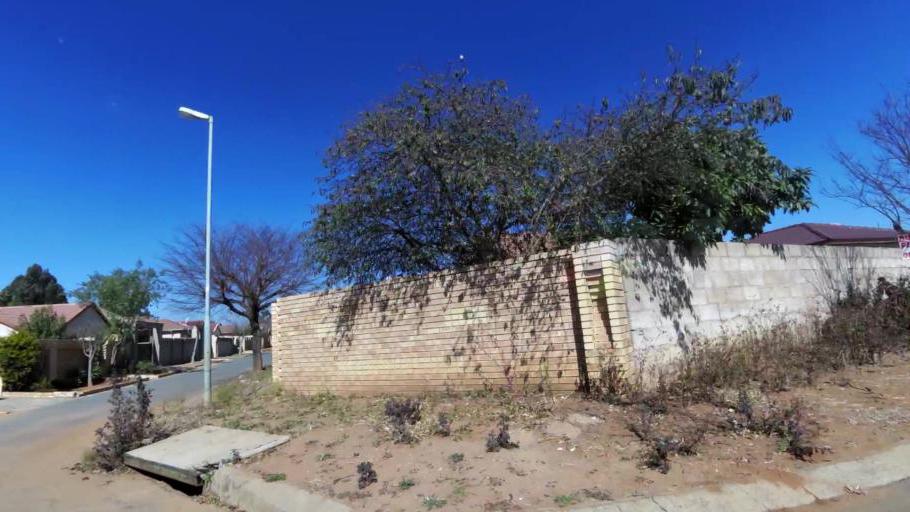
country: ZA
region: Gauteng
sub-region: City of Johannesburg Metropolitan Municipality
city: Johannesburg
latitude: -26.2480
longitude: 27.9804
